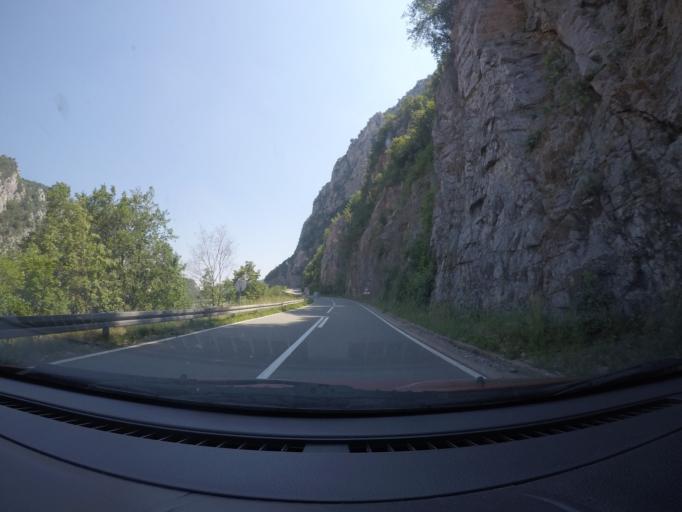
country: RO
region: Mehedinti
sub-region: Comuna Dubova
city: Dubova
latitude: 44.6287
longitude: 22.2860
